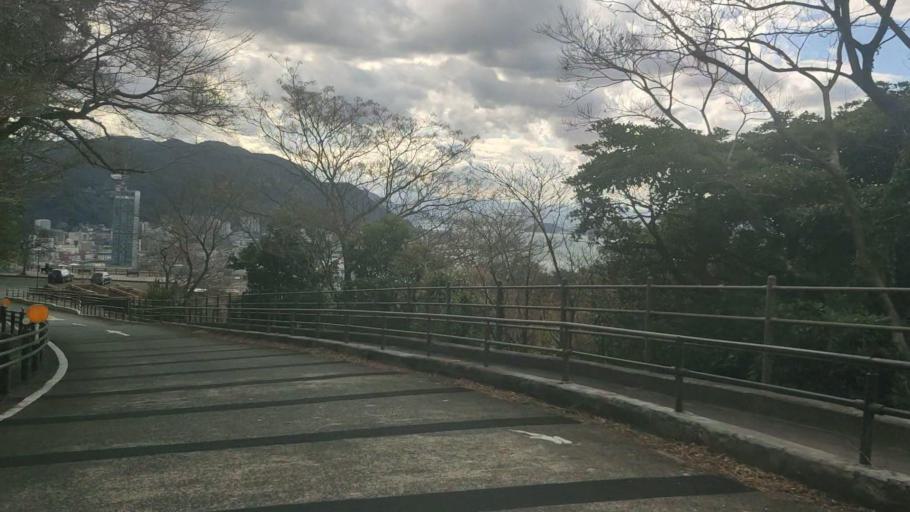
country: JP
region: Yamaguchi
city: Shimonoseki
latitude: 33.9590
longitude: 130.9675
